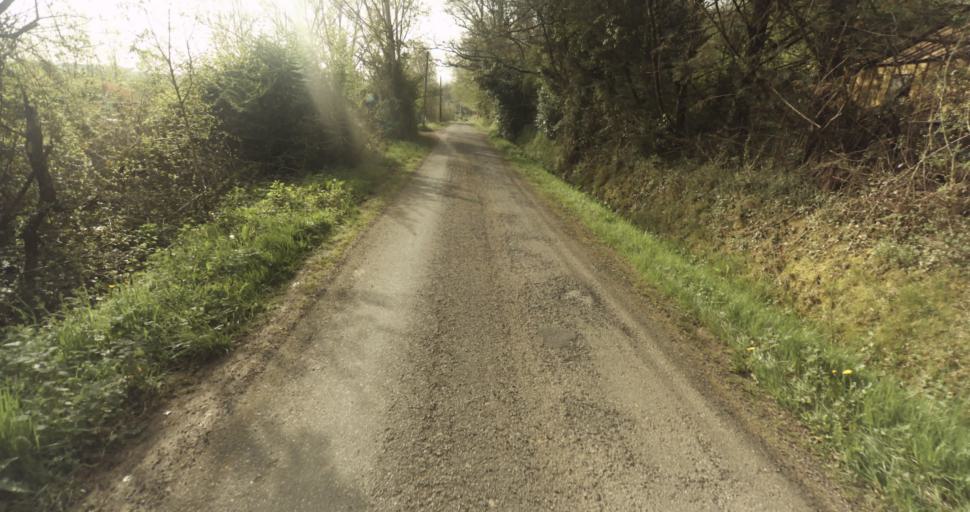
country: FR
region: Midi-Pyrenees
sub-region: Departement du Tarn-et-Garonne
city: Moissac
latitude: 44.1430
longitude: 1.0959
